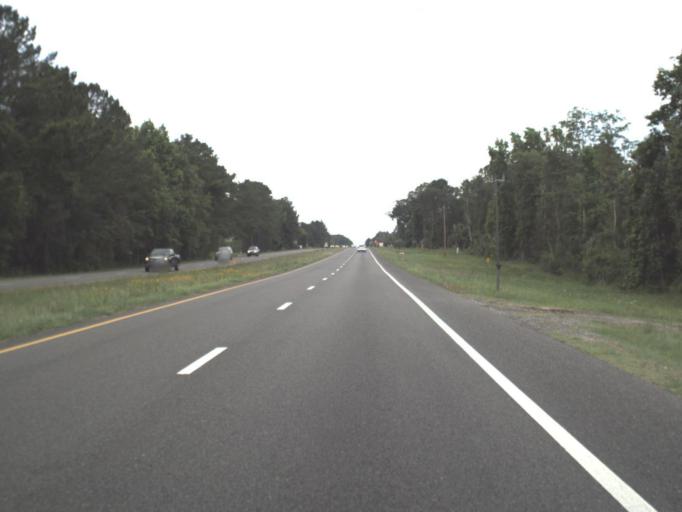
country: US
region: Florida
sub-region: Nassau County
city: Hilliard
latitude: 30.7138
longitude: -81.9335
